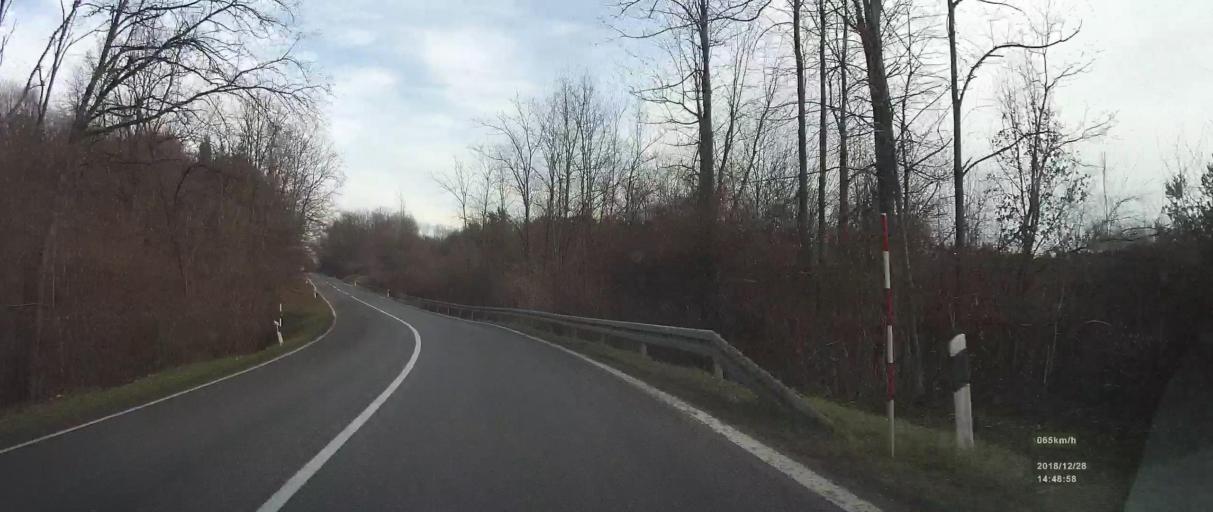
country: HR
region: Karlovacka
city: Ozalj
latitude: 45.4444
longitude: 15.3477
